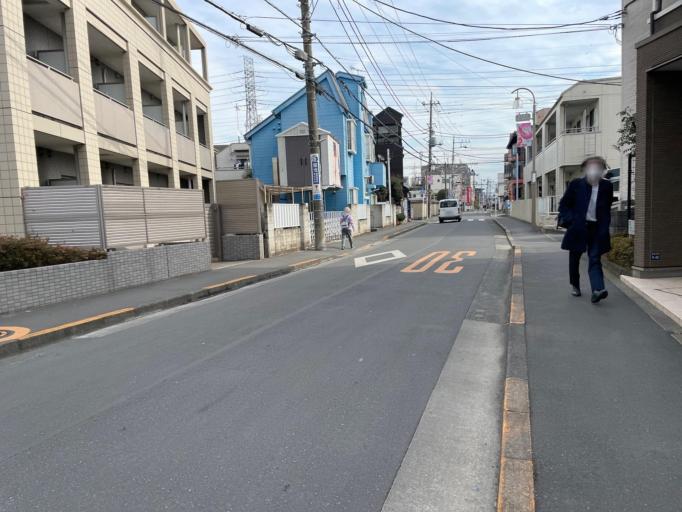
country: JP
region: Tokyo
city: Nishi-Tokyo-shi
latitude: 35.7007
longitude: 139.5277
